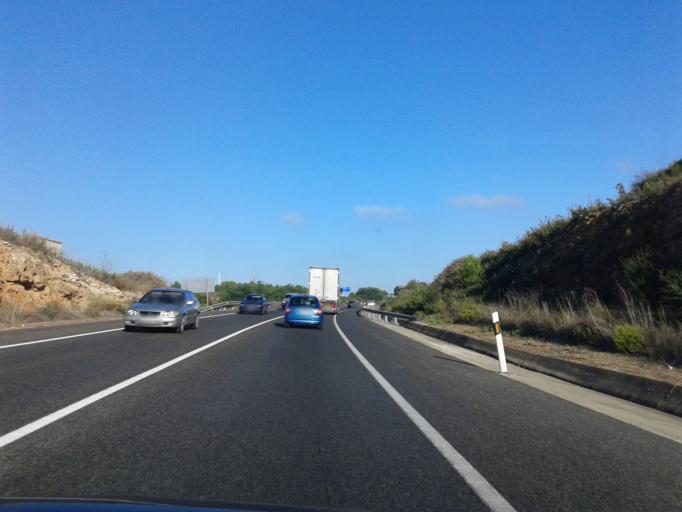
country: ES
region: Catalonia
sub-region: Provincia de Tarragona
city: Altafulla
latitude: 41.1561
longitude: 1.3730
